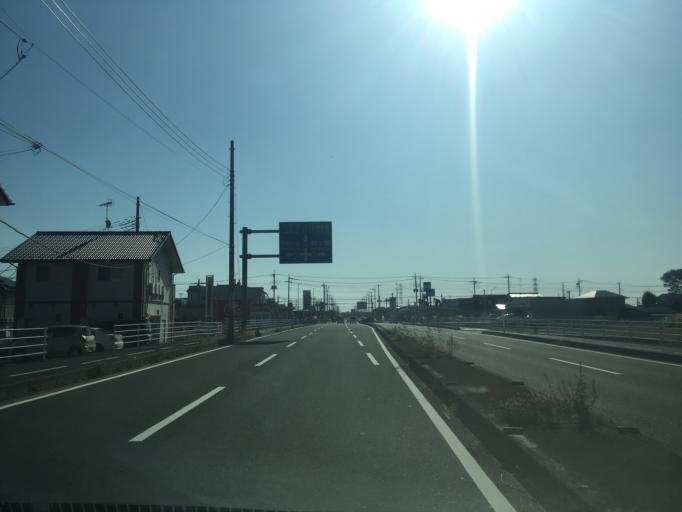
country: JP
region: Saitama
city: Kawagoe
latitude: 35.9330
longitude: 139.4684
